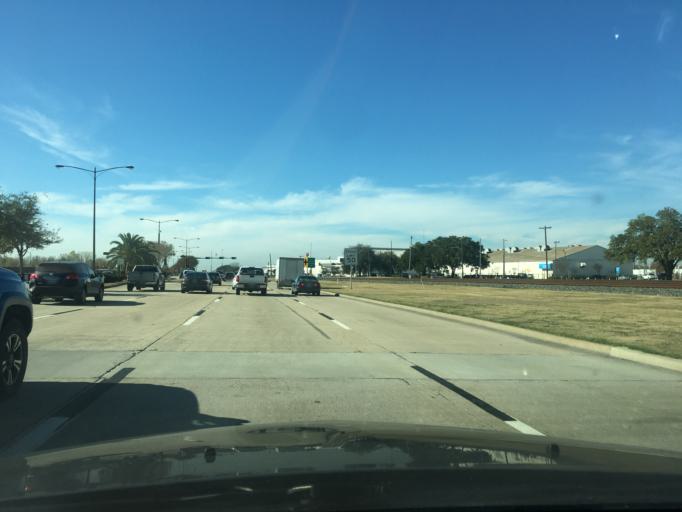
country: US
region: Texas
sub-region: Fort Bend County
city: Sugar Land
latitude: 29.6197
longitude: -95.6362
